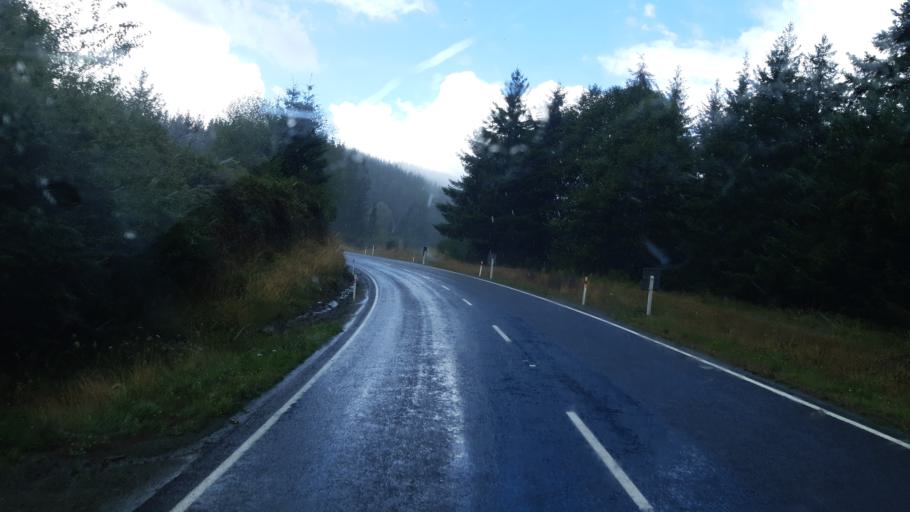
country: NZ
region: Tasman
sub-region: Tasman District
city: Wakefield
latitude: -41.4878
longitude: 172.8917
